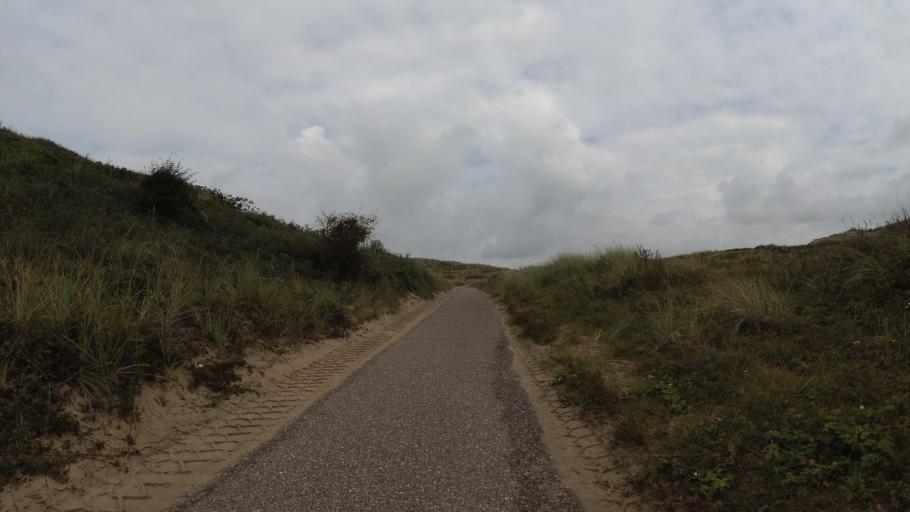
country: NL
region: North Holland
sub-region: Gemeente Den Helder
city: Den Helder
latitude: 52.9351
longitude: 4.7172
